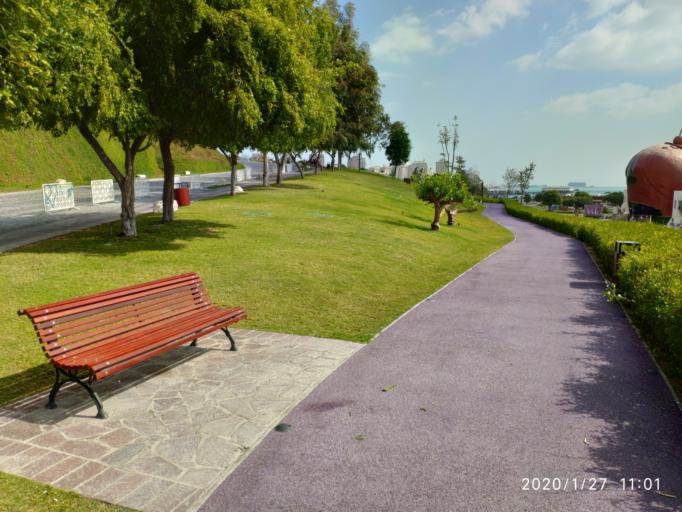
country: QA
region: Baladiyat ad Dawhah
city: Doha
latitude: 25.3627
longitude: 51.5248
